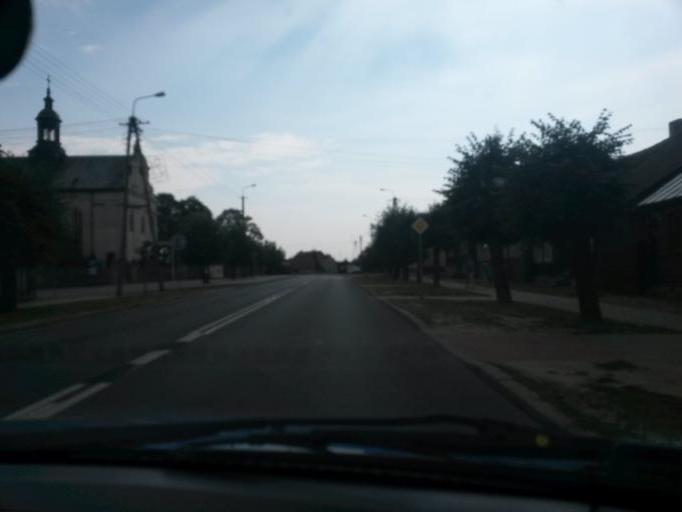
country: PL
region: Masovian Voivodeship
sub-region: Powiat zurominski
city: Biezun
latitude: 52.9593
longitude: 19.8926
